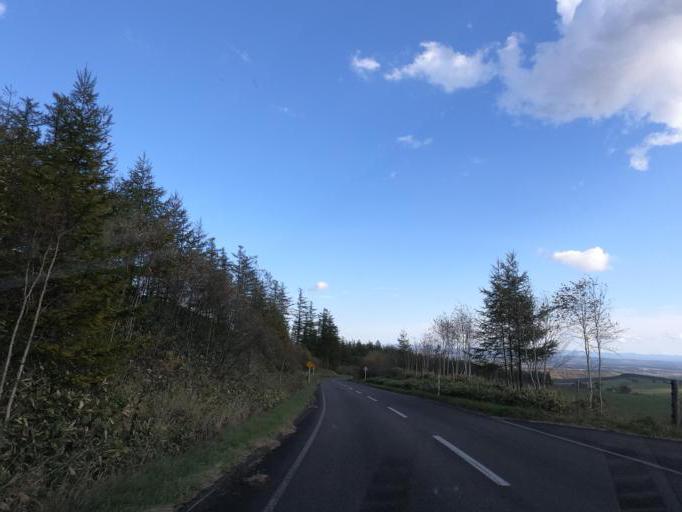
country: JP
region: Hokkaido
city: Otofuke
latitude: 43.2900
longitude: 143.2099
